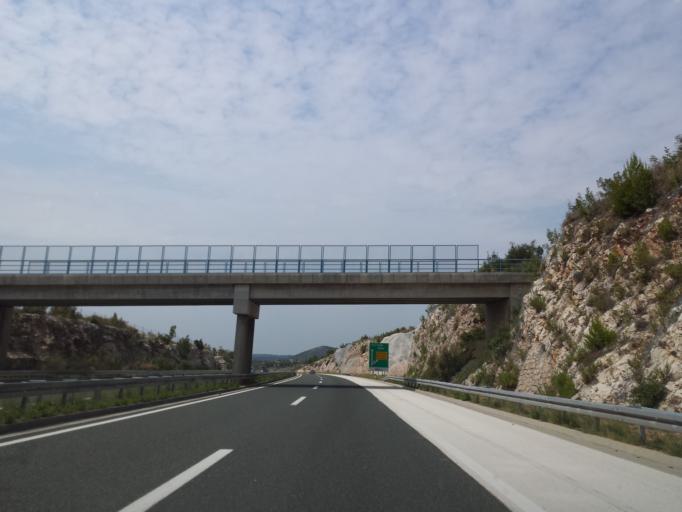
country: HR
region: Zadarska
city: Posedarje
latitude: 44.2197
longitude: 15.4704
